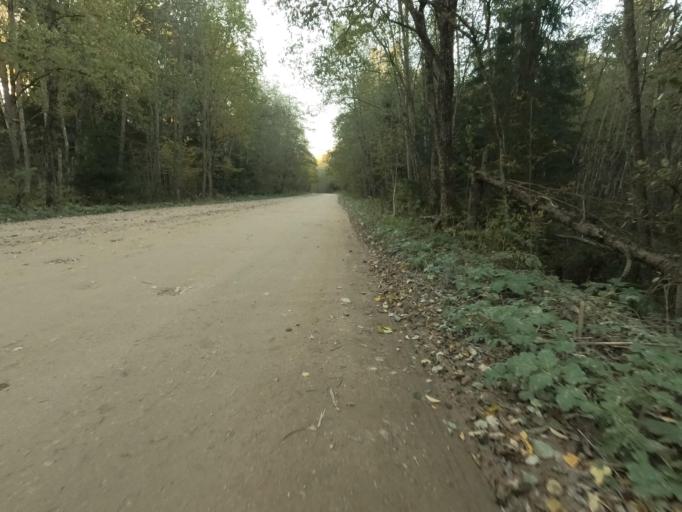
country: RU
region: Leningrad
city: Lyuban'
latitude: 59.0043
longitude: 31.0960
